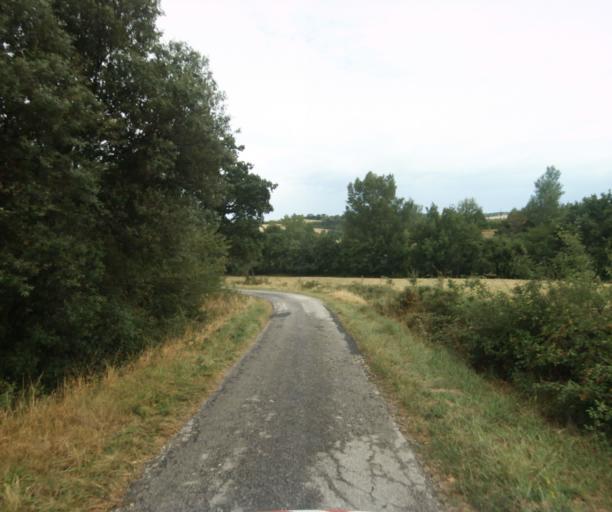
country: FR
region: Midi-Pyrenees
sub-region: Departement de la Haute-Garonne
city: Revel
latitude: 43.4202
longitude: 1.9779
